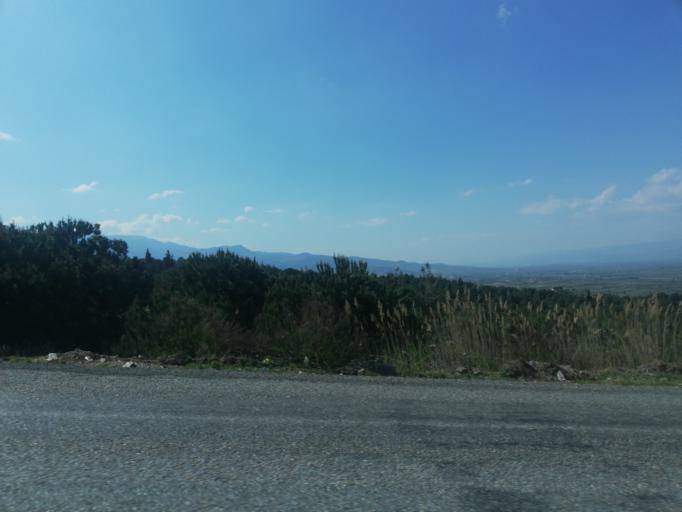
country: TR
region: Manisa
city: Sarigol
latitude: 38.2154
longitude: 28.6616
